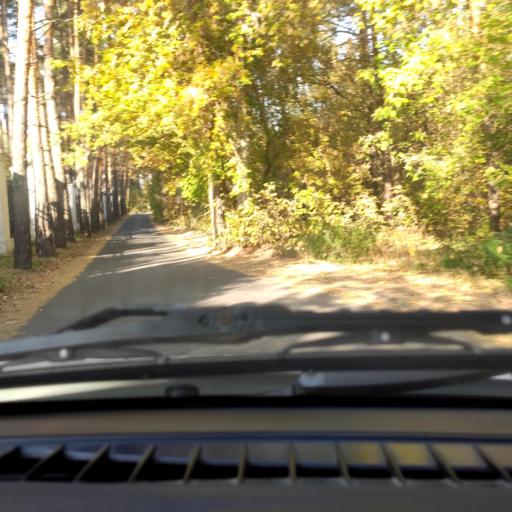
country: RU
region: Samara
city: Tol'yatti
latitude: 53.4764
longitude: 49.3578
